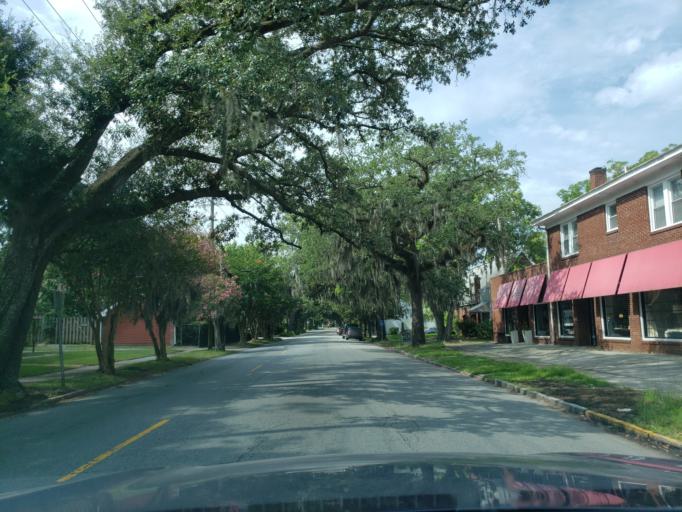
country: US
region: Georgia
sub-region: Chatham County
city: Thunderbolt
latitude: 32.0436
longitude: -81.0869
